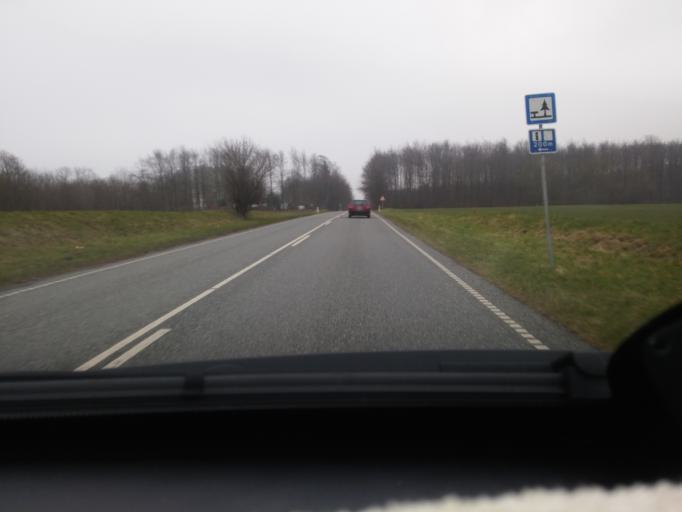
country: DK
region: South Denmark
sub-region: Kerteminde Kommune
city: Kerteminde
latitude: 55.4379
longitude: 10.6847
